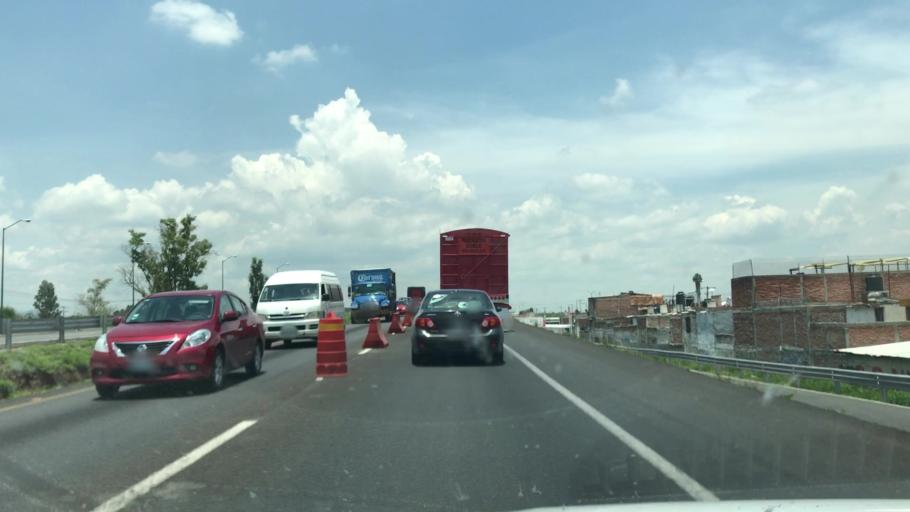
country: MX
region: Guanajuato
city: Irapuato
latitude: 20.6498
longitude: -101.3441
